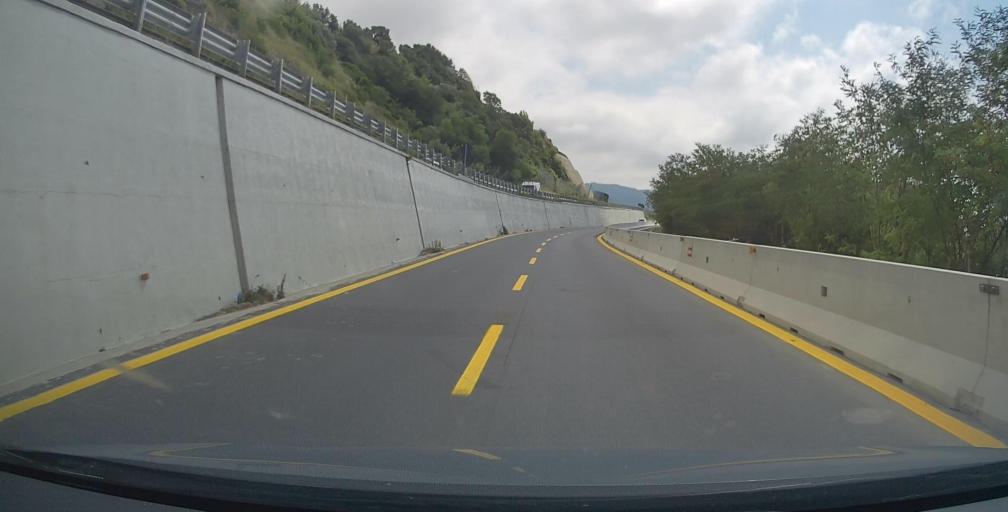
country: IT
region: Calabria
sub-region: Provincia di Vibo-Valentia
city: Pizzo
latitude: 38.7642
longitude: 16.2045
